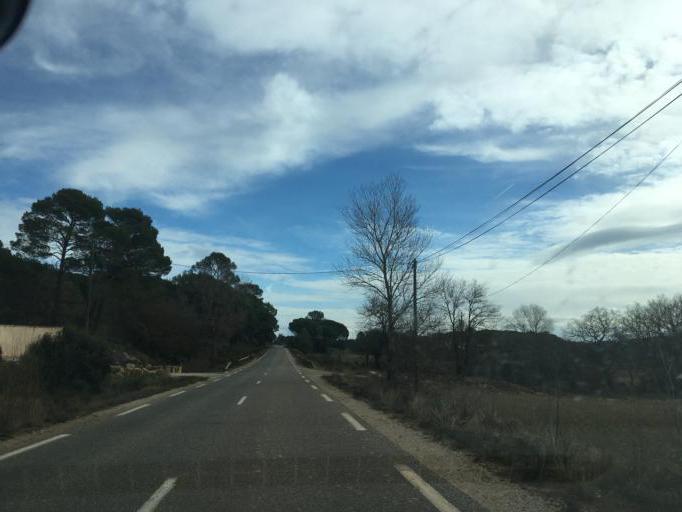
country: FR
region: Provence-Alpes-Cote d'Azur
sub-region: Departement du Var
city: La Celle
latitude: 43.4455
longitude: 6.0108
